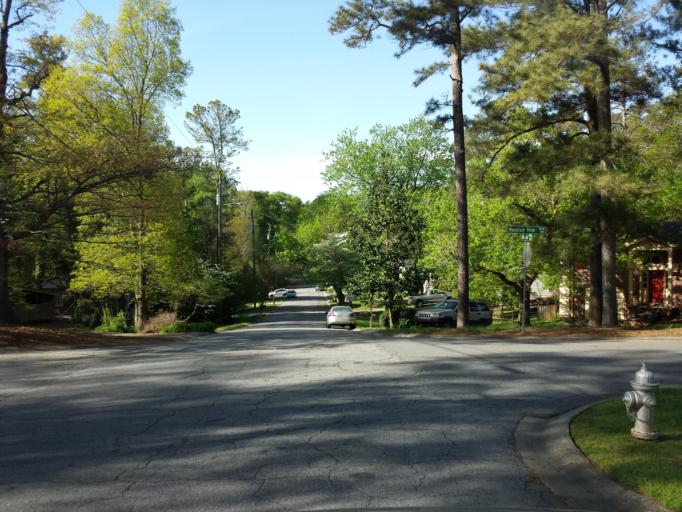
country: US
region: Georgia
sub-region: Cobb County
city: Marietta
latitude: 33.9673
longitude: -84.5209
